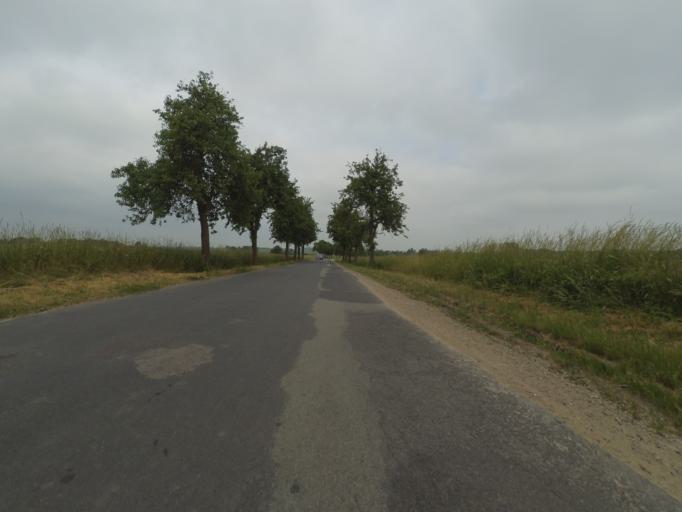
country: DE
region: Mecklenburg-Vorpommern
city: Goldberg
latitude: 53.5106
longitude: 12.1193
